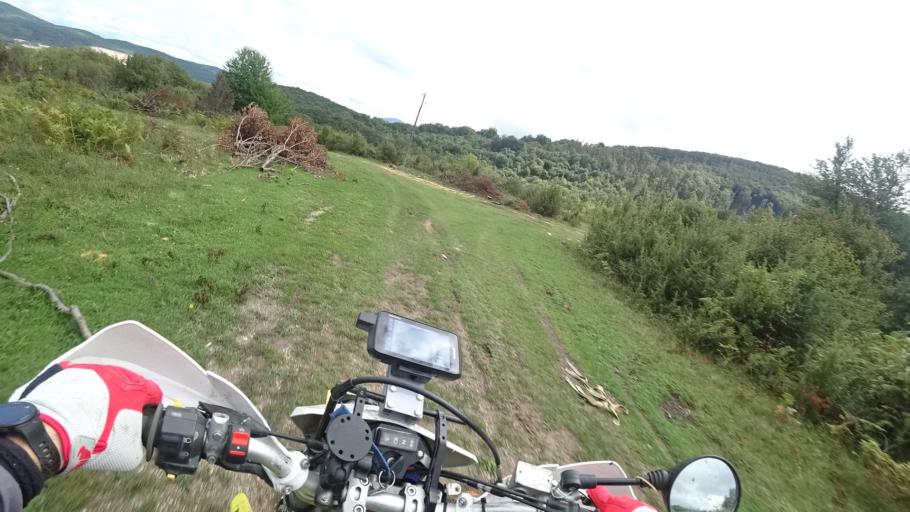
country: BA
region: Republika Srpska
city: Bronzani Majdan
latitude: 44.6459
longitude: 17.0133
